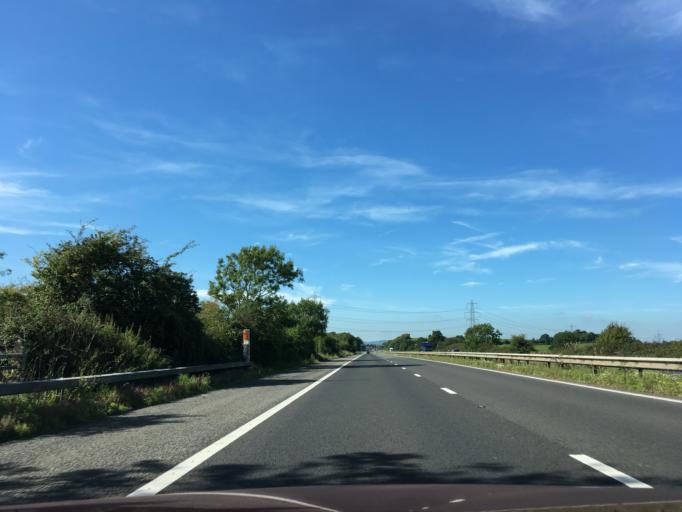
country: GB
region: England
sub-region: South Gloucestershire
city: Almondsbury
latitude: 51.5811
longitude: -2.5921
